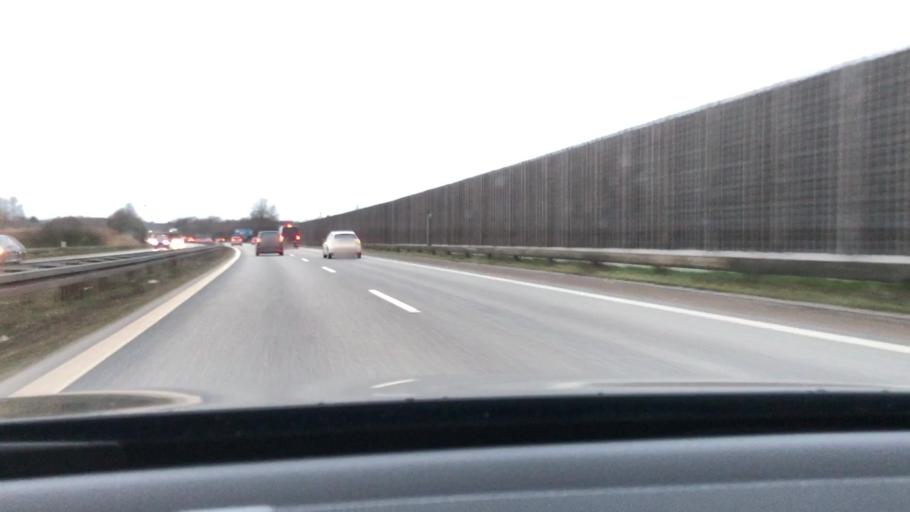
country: DK
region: Central Jutland
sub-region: Randers Kommune
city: Randers
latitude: 56.4201
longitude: 10.0674
